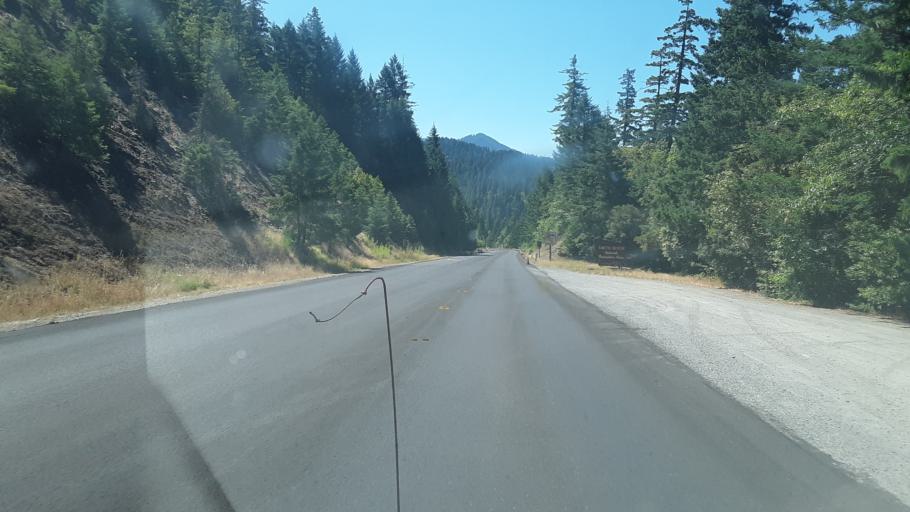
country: US
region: Oregon
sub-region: Josephine County
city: Cave Junction
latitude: 41.9643
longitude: -123.7469
